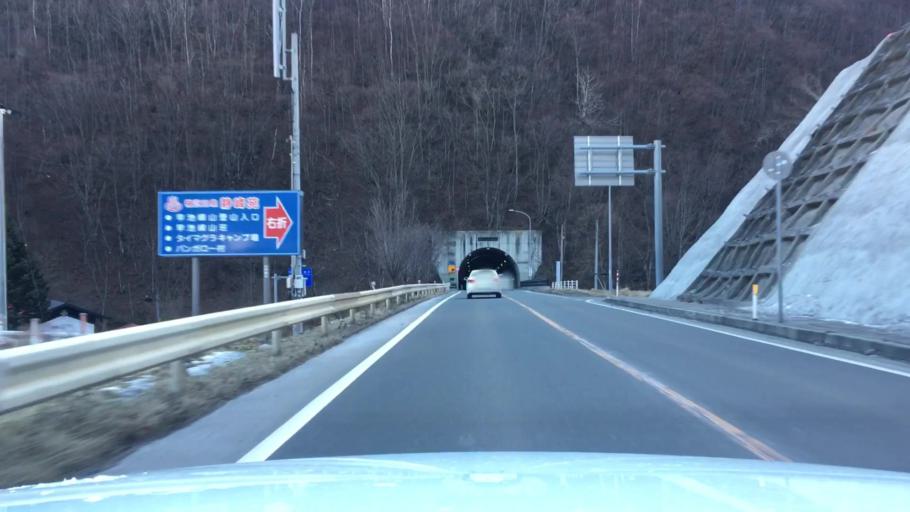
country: JP
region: Iwate
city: Tono
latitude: 39.6226
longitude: 141.6146
